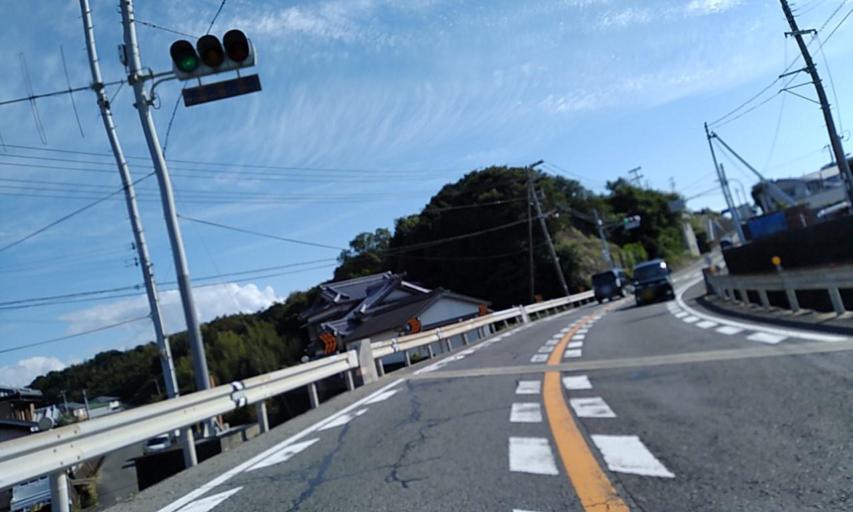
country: JP
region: Wakayama
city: Gobo
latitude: 33.8083
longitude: 135.2212
